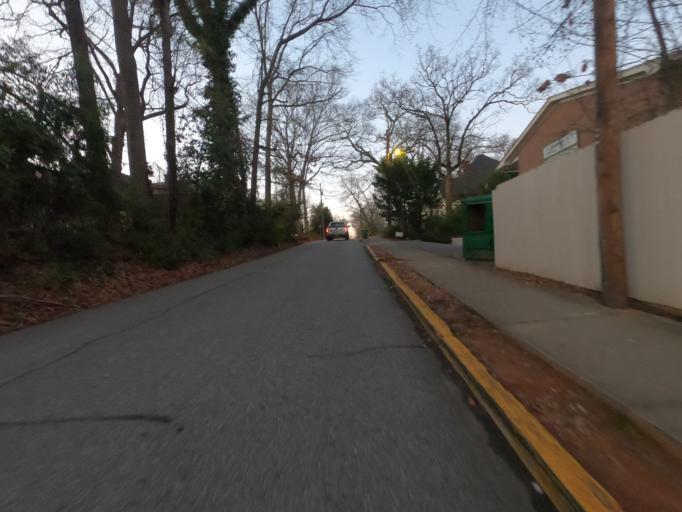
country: US
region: Georgia
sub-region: Clarke County
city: Athens
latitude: 33.9506
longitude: -83.3839
